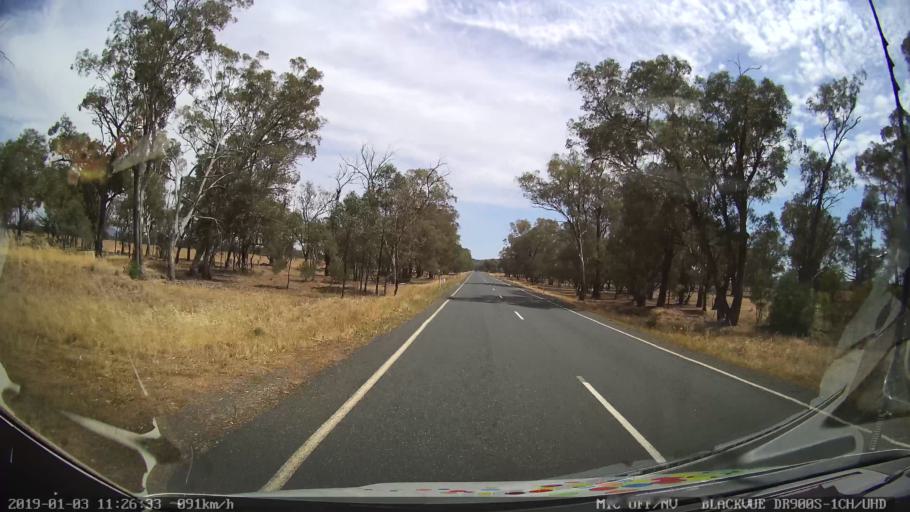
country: AU
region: New South Wales
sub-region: Weddin
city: Grenfell
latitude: -34.0236
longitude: 148.2245
